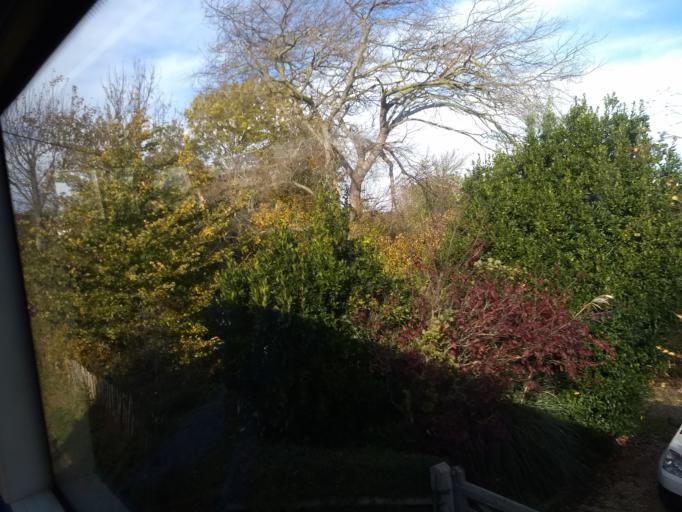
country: GB
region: England
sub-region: Isle of Wight
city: Shalfleet
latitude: 50.6926
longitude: -1.4573
